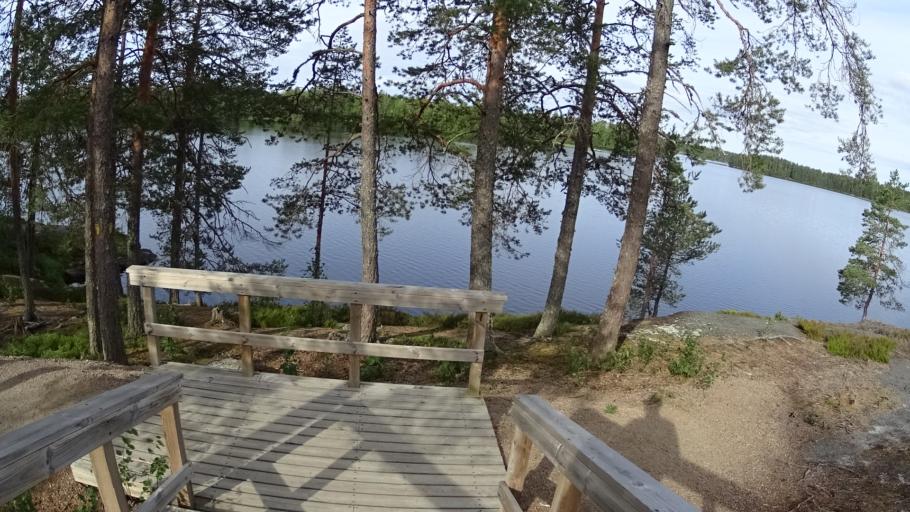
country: FI
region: Southern Ostrobothnia
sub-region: Kuusiokunnat
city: AEhtaeri
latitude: 62.5356
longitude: 24.1793
